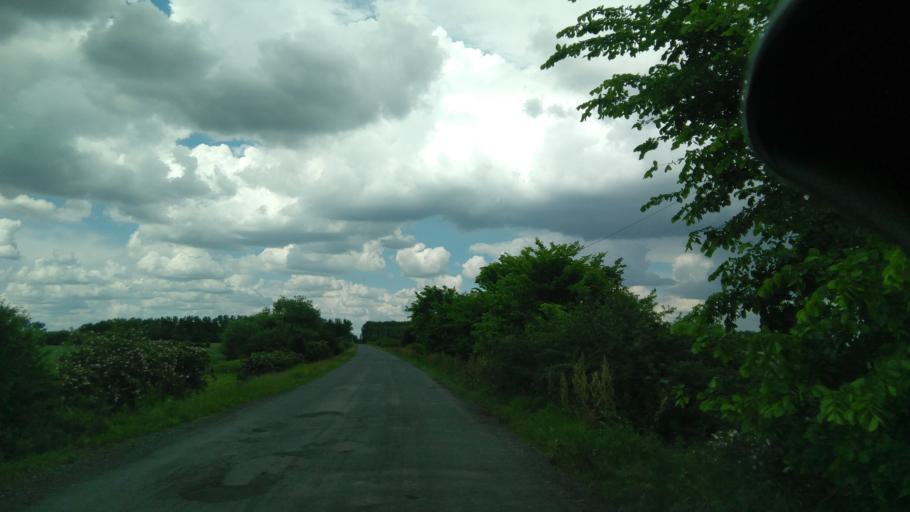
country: HU
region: Bekes
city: Szeghalom
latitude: 47.1105
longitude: 21.0876
